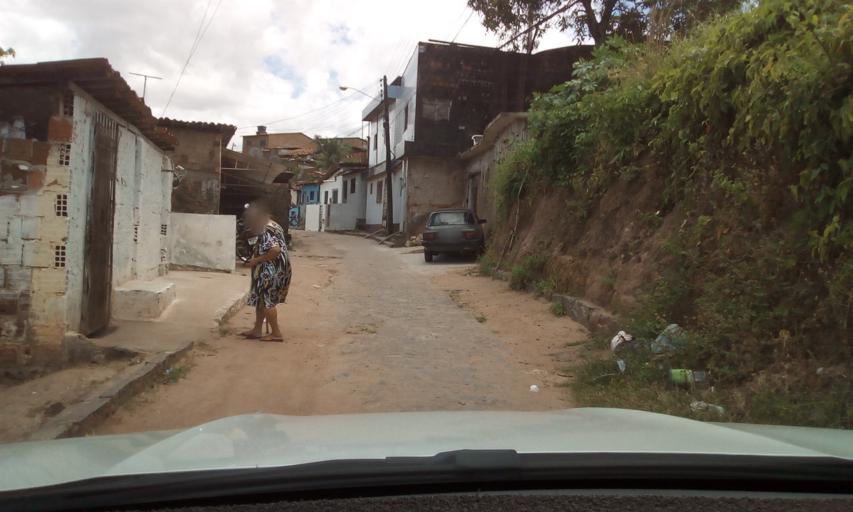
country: BR
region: Paraiba
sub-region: Joao Pessoa
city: Joao Pessoa
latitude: -7.1254
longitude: -34.8887
